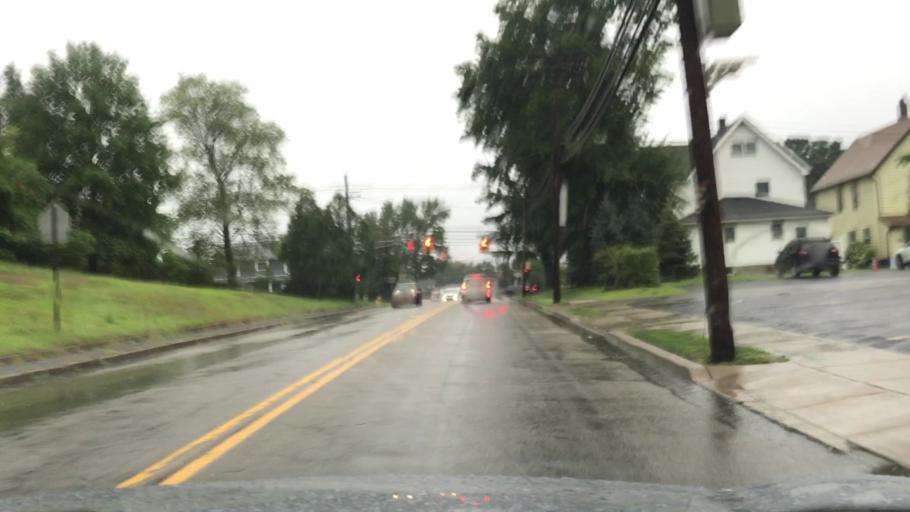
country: US
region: New Jersey
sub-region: Bergen County
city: Closter
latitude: 40.9712
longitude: -73.9633
